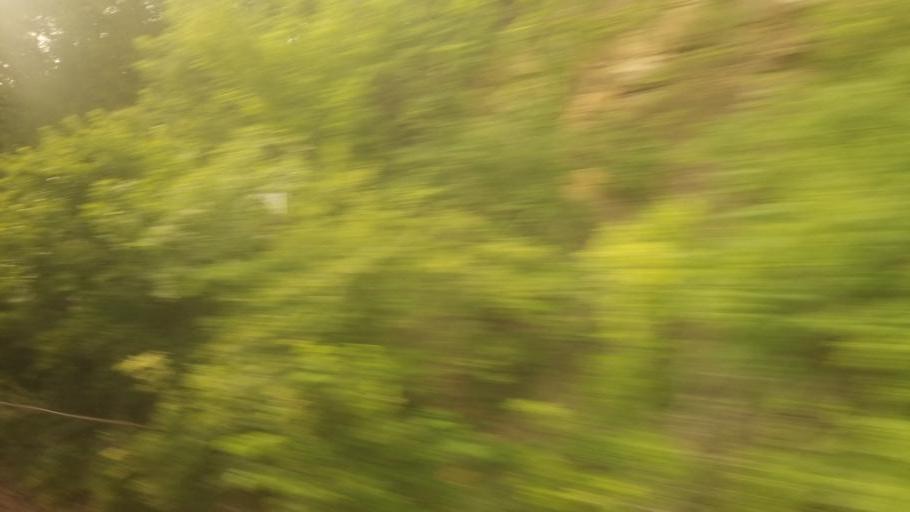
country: US
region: Kansas
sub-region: Shawnee County
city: Topeka
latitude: 39.0527
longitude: -95.4945
